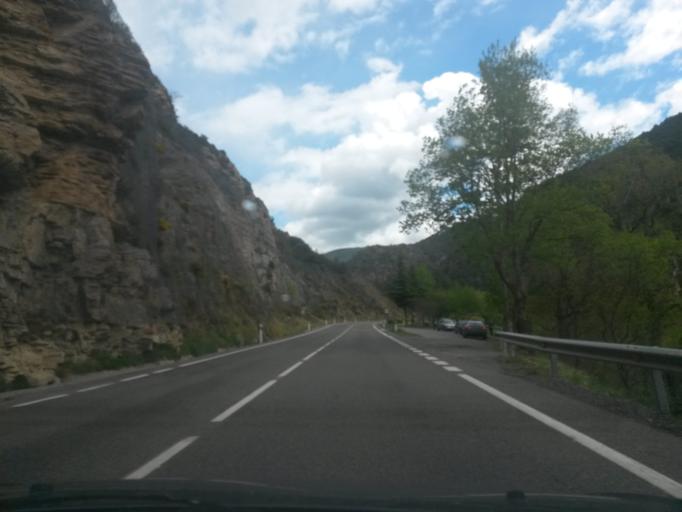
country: ES
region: Catalonia
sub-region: Provincia de Lleida
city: Alas i Cerc
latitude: 42.3587
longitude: 1.5468
